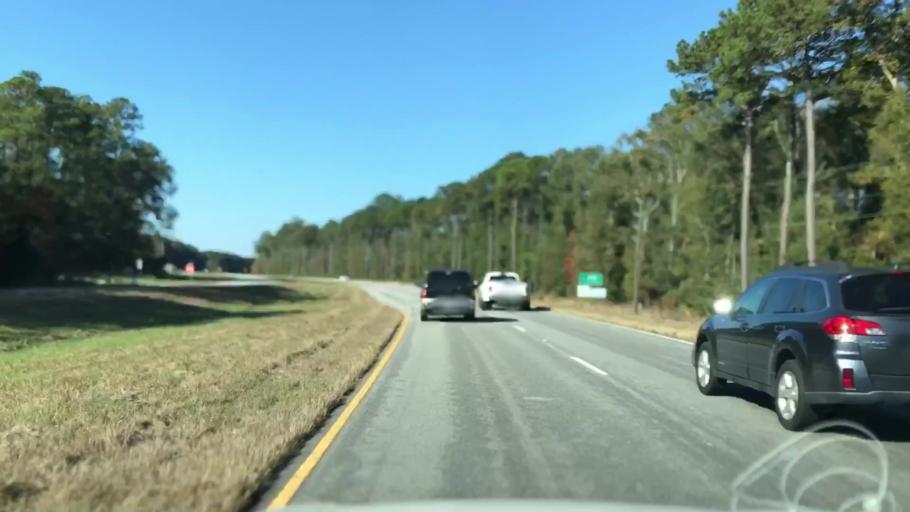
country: US
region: South Carolina
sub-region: Charleston County
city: Ravenel
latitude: 32.7599
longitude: -80.3879
